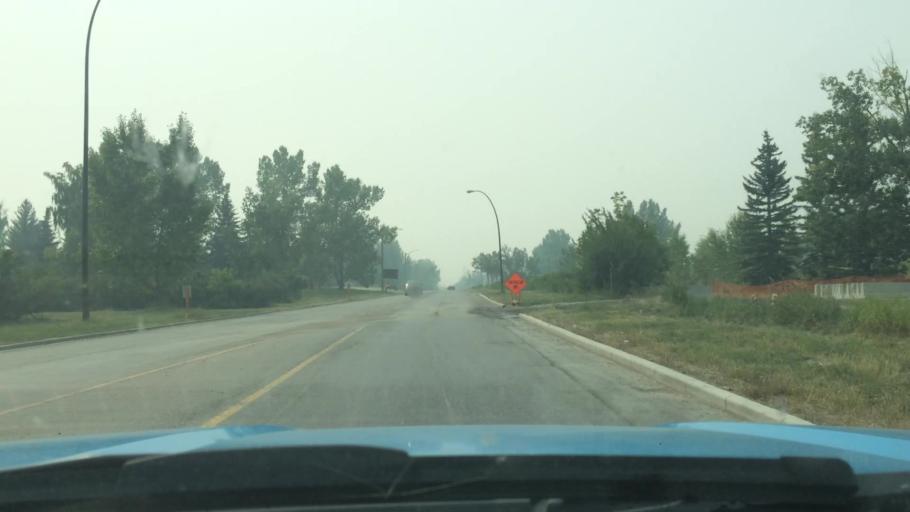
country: CA
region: Alberta
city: Calgary
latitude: 50.9487
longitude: -114.0948
